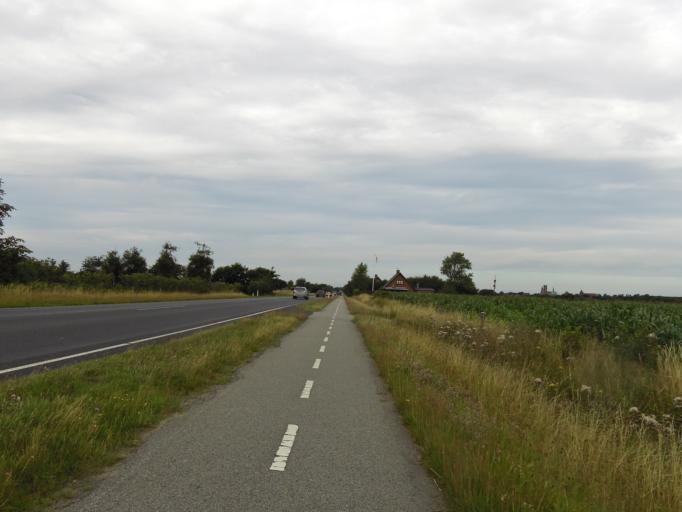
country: DK
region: South Denmark
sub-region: Esbjerg Kommune
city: Ribe
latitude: 55.3156
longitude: 8.7826
